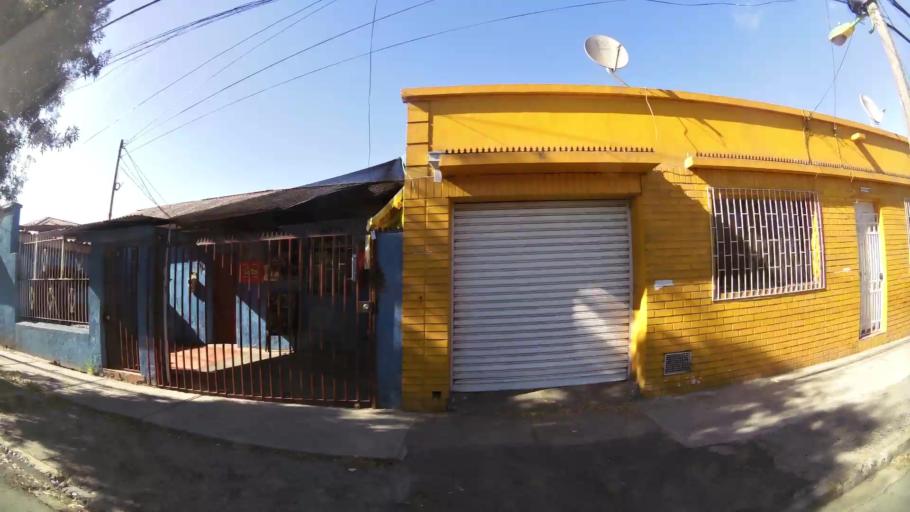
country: CL
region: Santiago Metropolitan
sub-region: Provincia de Maipo
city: San Bernardo
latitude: -33.5512
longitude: -70.6794
